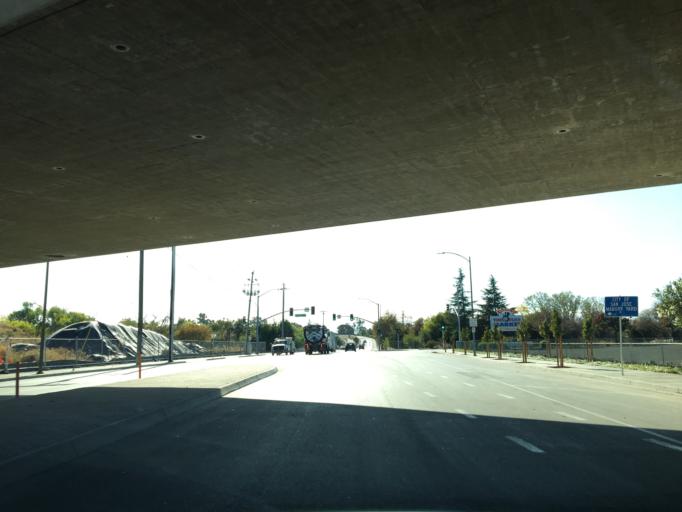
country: US
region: California
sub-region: Santa Clara County
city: San Jose
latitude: 37.3644
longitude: -121.8732
